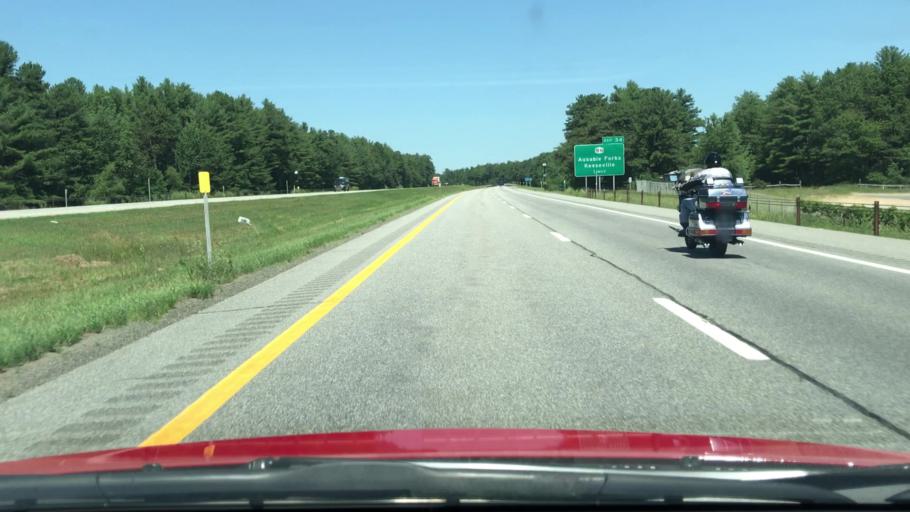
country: US
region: New York
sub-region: Essex County
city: Keeseville
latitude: 44.4799
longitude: -73.4888
